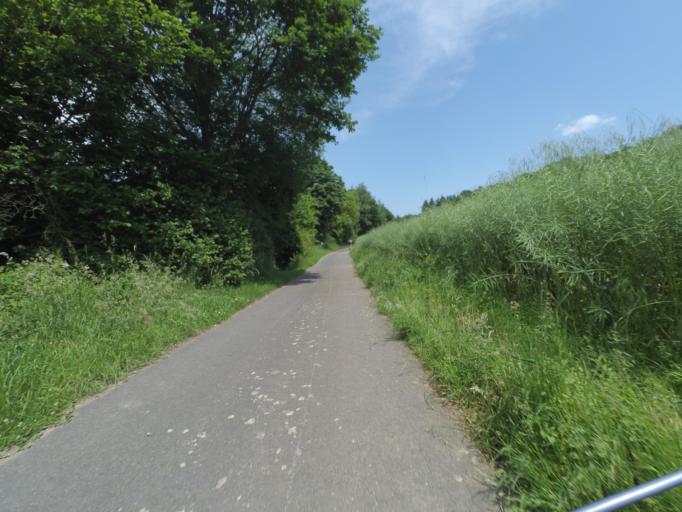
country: DE
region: Rheinland-Pfalz
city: Morshausen
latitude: 50.1951
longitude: 7.4397
